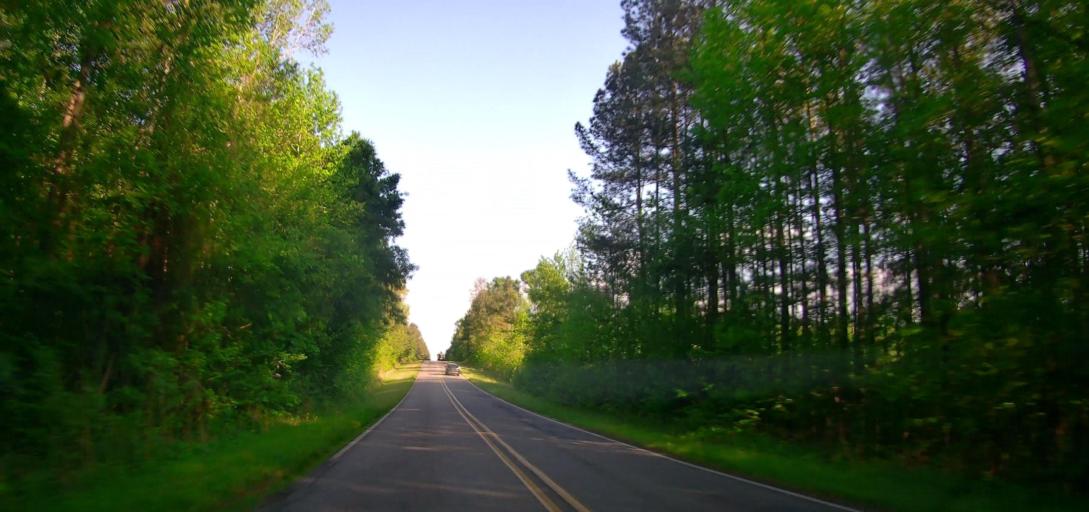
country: US
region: Georgia
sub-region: Putnam County
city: Eatonton
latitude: 33.2789
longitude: -83.3134
